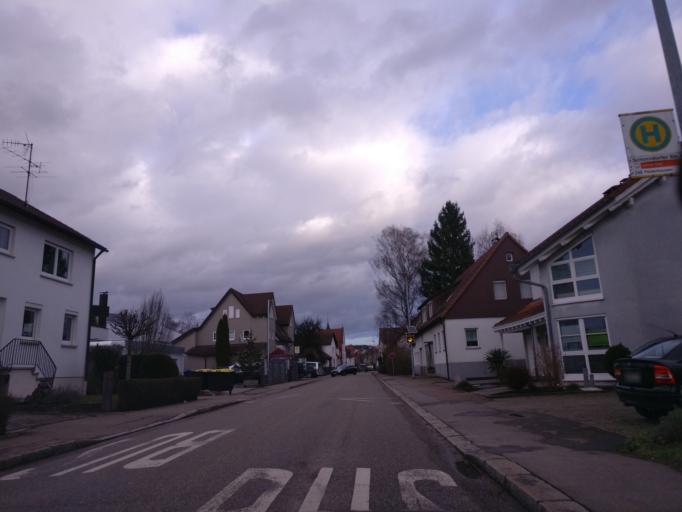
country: DE
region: Baden-Wuerttemberg
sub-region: Regierungsbezirk Stuttgart
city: Urbach
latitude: 48.8096
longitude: 9.5739
